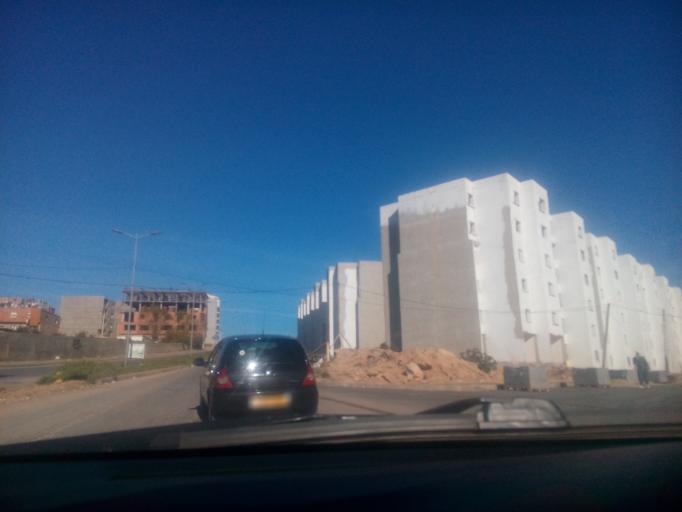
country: DZ
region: Oran
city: Bir el Djir
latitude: 35.7438
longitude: -0.5483
